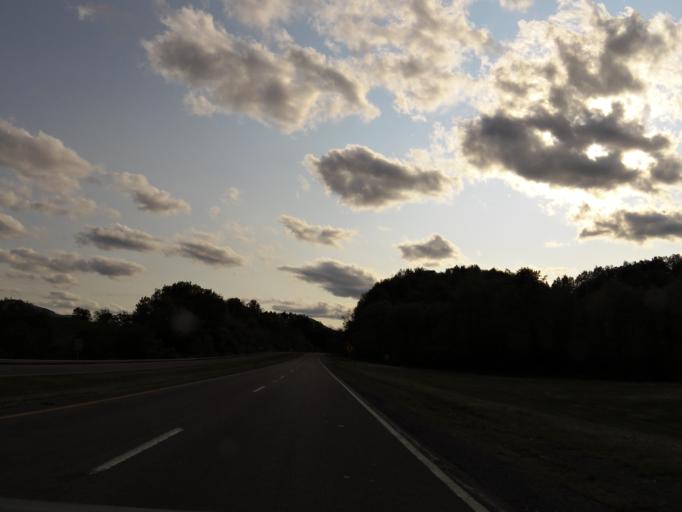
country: US
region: Virginia
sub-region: Tazewell County
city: Tazewell
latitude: 37.1214
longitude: -81.5472
